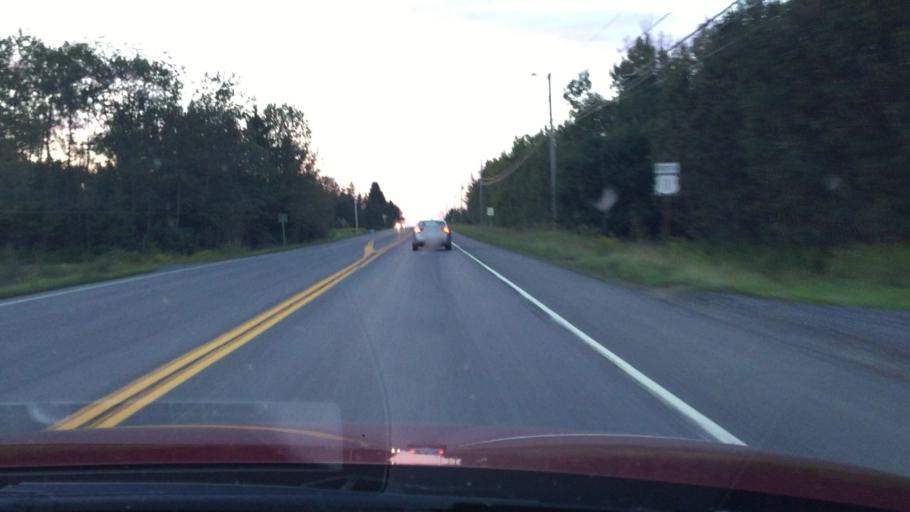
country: US
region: Maine
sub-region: Aroostook County
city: Easton
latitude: 46.5697
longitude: -67.9507
